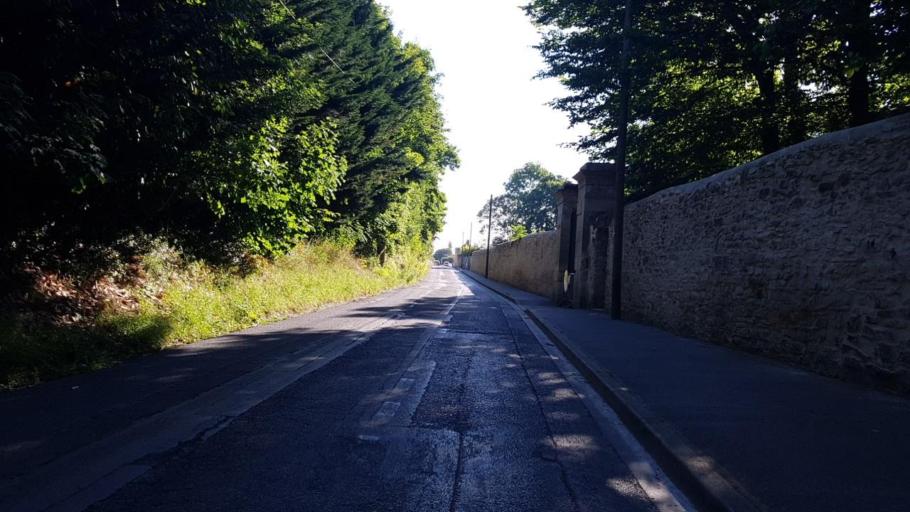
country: FR
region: Picardie
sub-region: Departement de l'Oise
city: Senlis
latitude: 49.2145
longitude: 2.5934
